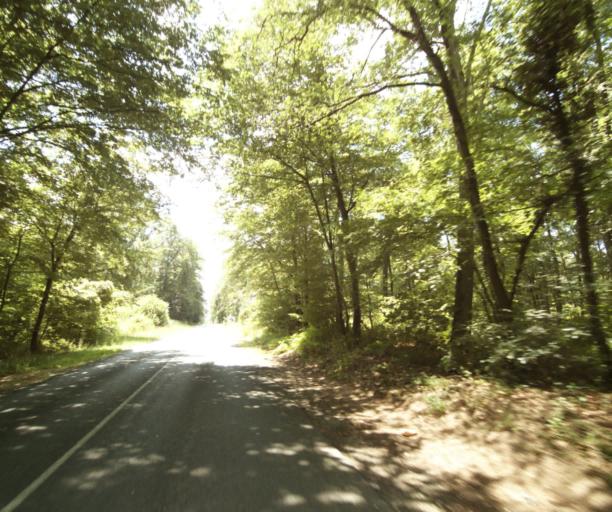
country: FR
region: Ile-de-France
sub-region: Departement de Seine-et-Marne
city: Samoreau
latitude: 48.4361
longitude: 2.7419
